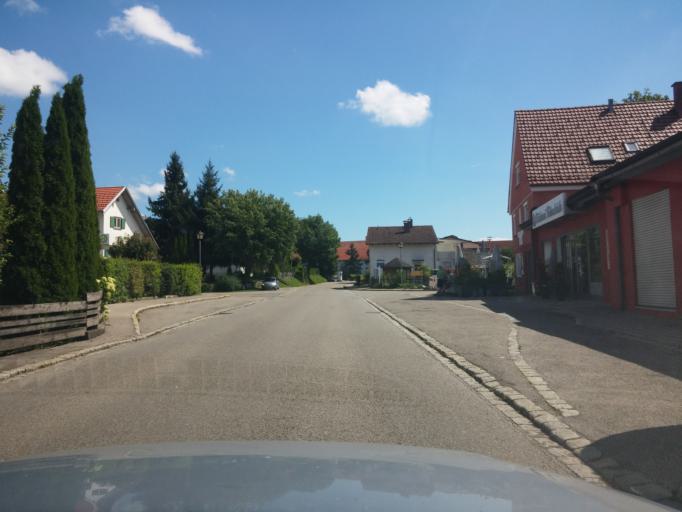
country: DE
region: Bavaria
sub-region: Swabia
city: Woringen
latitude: 47.8791
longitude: 10.2181
